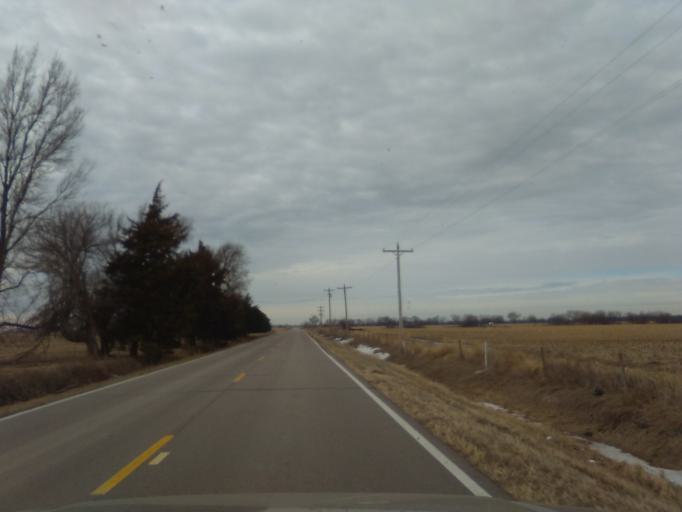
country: US
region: Nebraska
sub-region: Hall County
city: Grand Island
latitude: 40.7710
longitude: -98.4215
